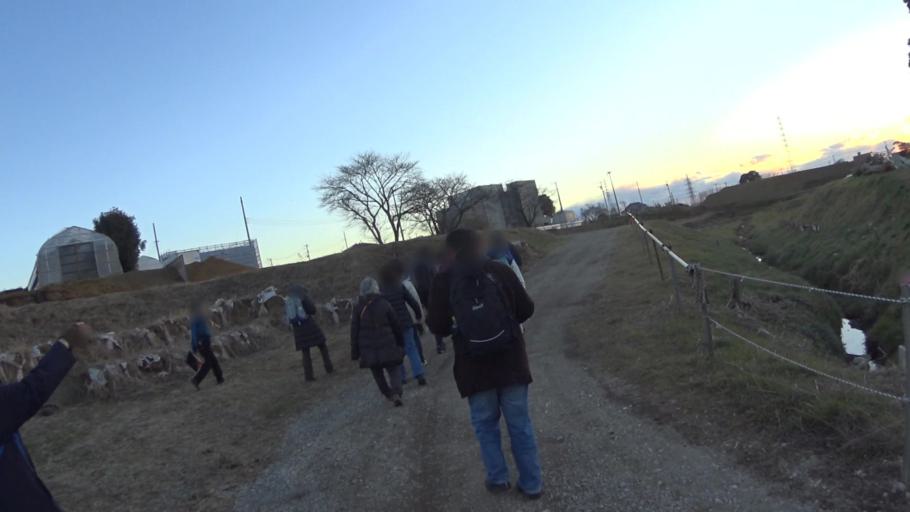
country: JP
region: Saitama
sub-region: Kawaguchi-shi
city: Hatogaya-honcho
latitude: 35.8775
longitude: 139.7388
